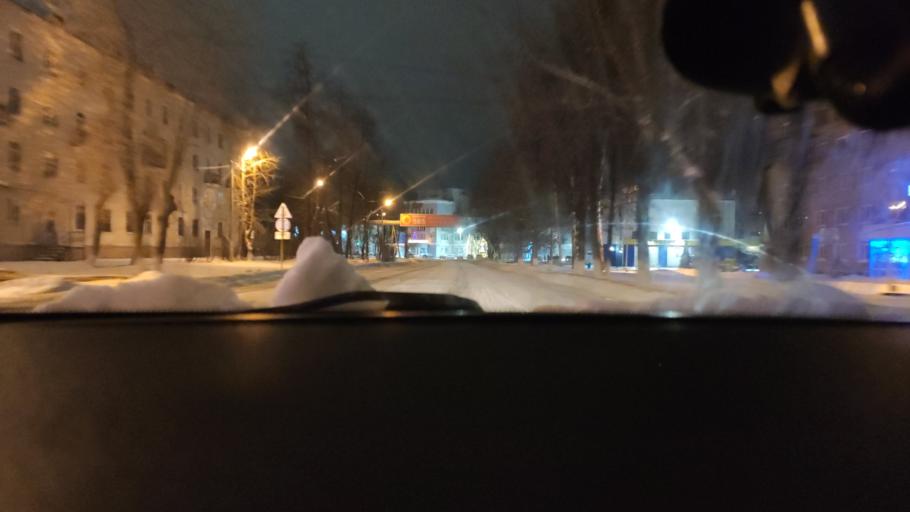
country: RU
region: Perm
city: Krasnokamsk
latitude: 58.0779
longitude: 55.7526
